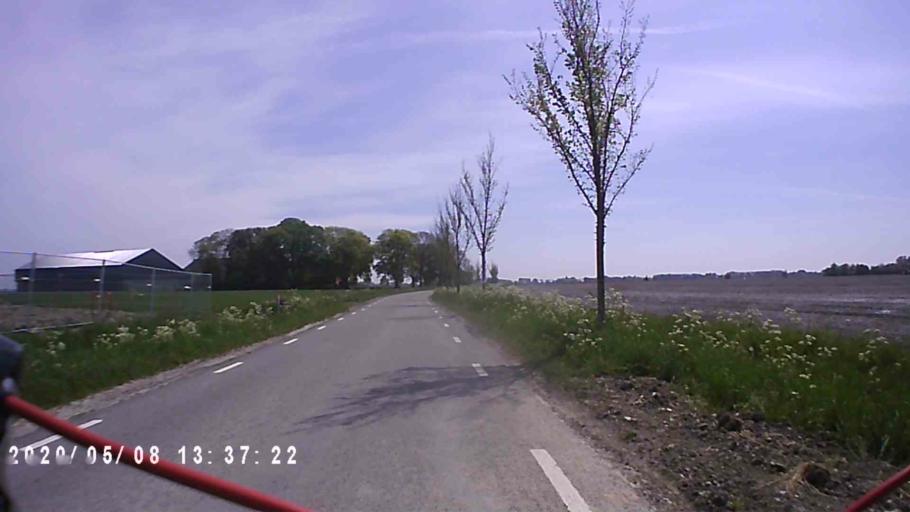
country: NL
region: Groningen
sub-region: Gemeente Appingedam
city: Appingedam
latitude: 53.3301
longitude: 6.7620
